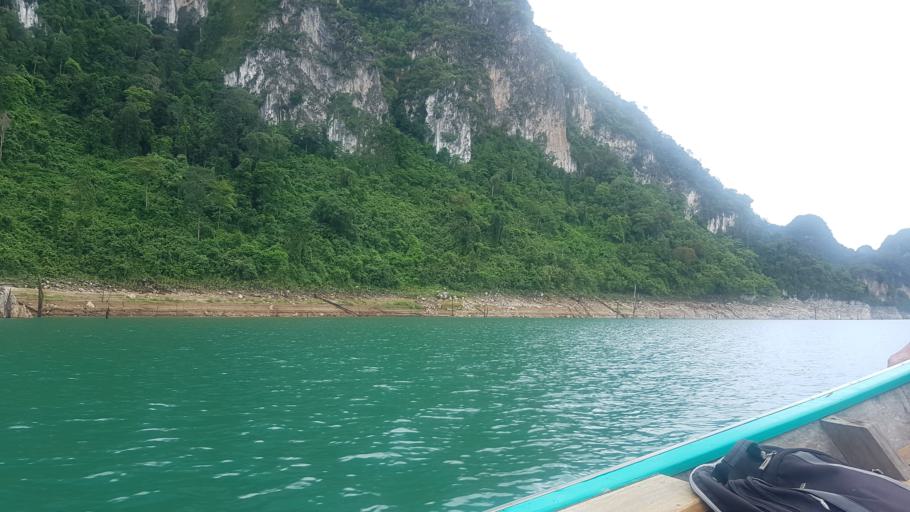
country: TH
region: Surat Thani
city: Phanom
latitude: 9.0312
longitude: 98.7184
